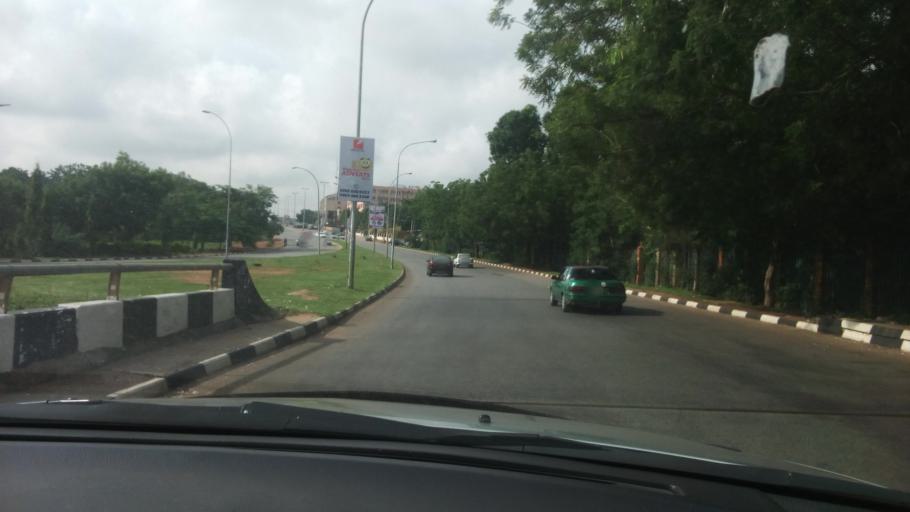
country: NG
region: Abuja Federal Capital Territory
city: Abuja
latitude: 9.0696
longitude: 7.4954
